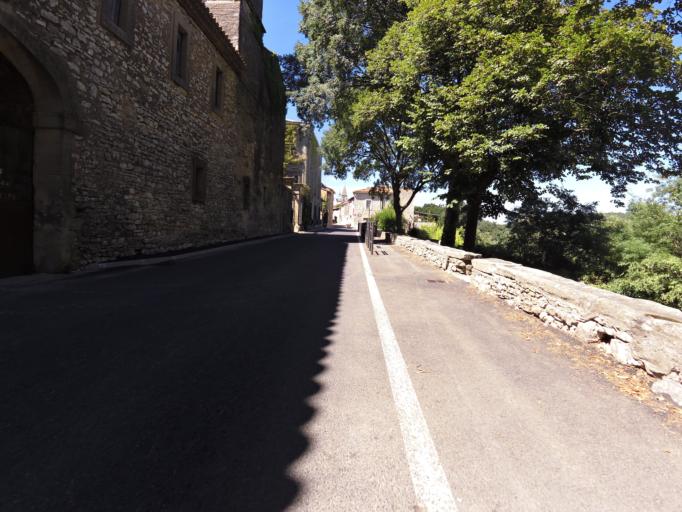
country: FR
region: Languedoc-Roussillon
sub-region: Departement du Gard
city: Sommieres
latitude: 43.8087
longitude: 4.0693
